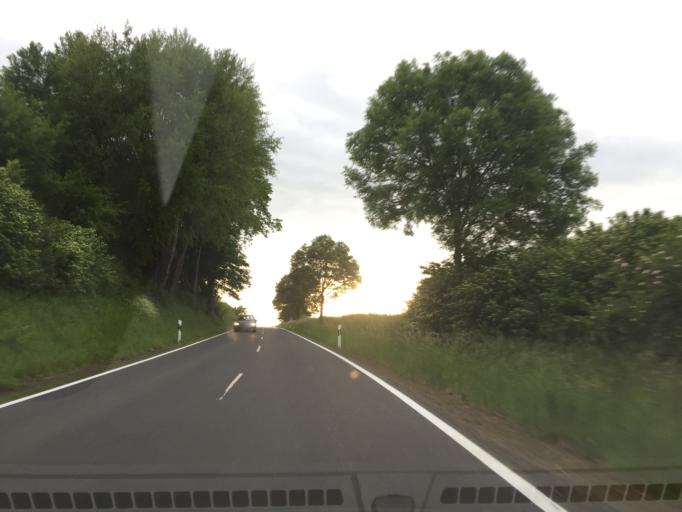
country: DE
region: Rheinland-Pfalz
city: Hundsangen
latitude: 50.4541
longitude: 8.0104
